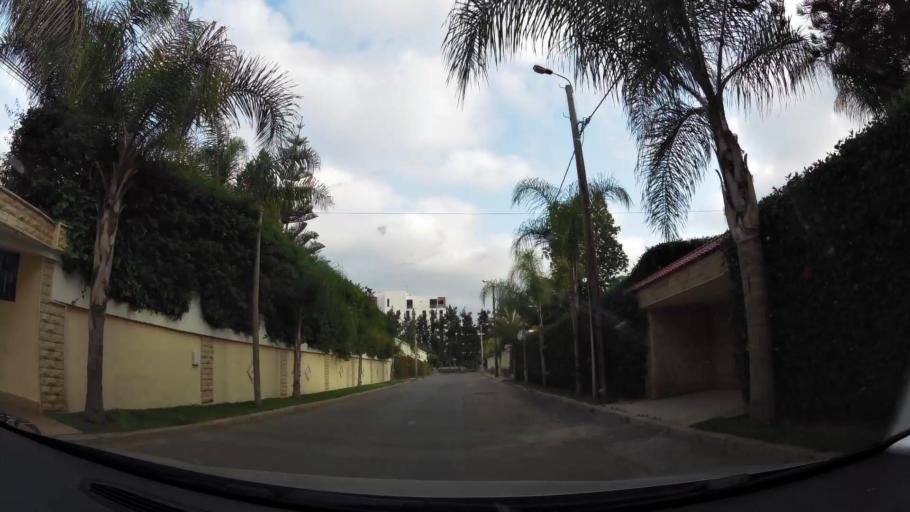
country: MA
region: Rabat-Sale-Zemmour-Zaer
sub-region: Rabat
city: Rabat
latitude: 33.9524
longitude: -6.8355
